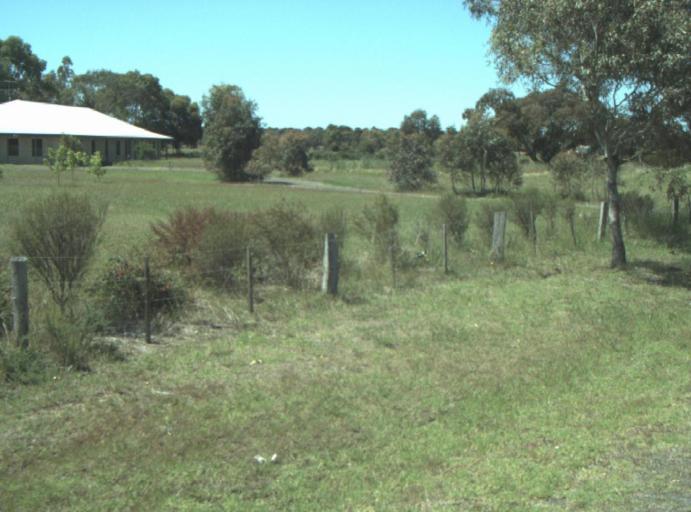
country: AU
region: Victoria
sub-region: Greater Geelong
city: Breakwater
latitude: -38.2099
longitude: 144.3587
